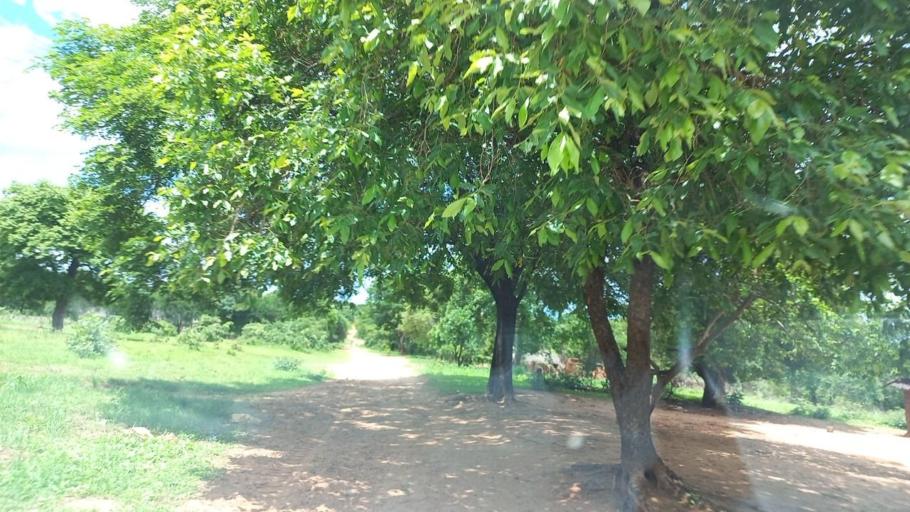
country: ZM
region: North-Western
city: Kabompo
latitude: -13.6105
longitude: 24.2446
